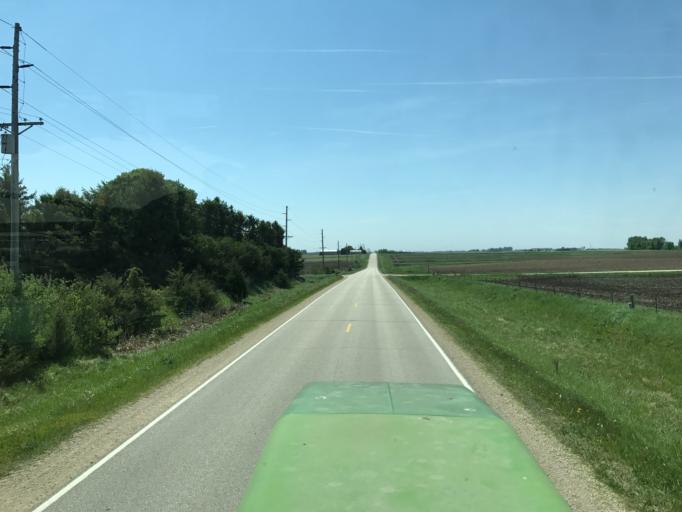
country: US
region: Iowa
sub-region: Butler County
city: Shell Rock
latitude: 42.6726
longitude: -92.5936
